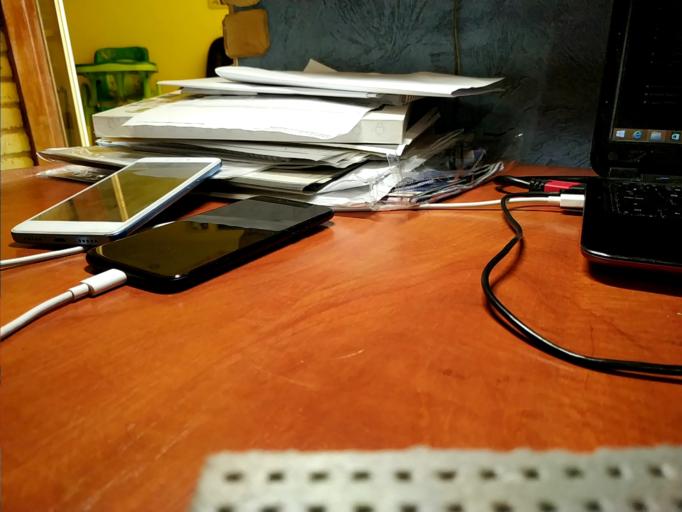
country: RU
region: Tverskaya
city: Spirovo
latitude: 57.4248
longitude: 35.0815
